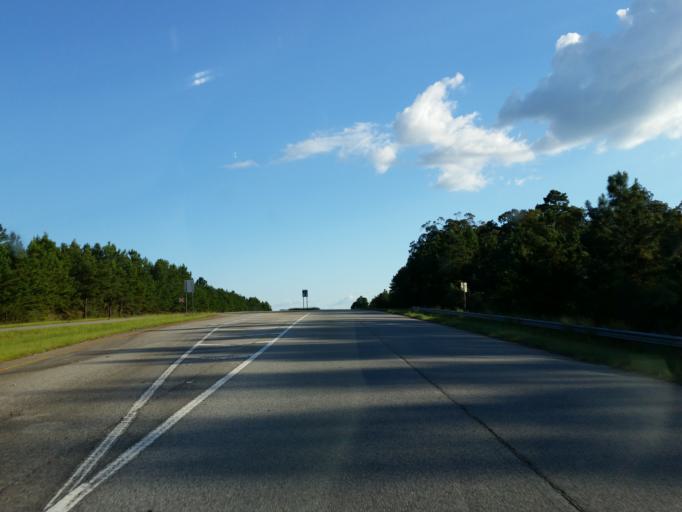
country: US
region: Georgia
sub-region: Houston County
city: Perry
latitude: 32.4709
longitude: -83.7781
